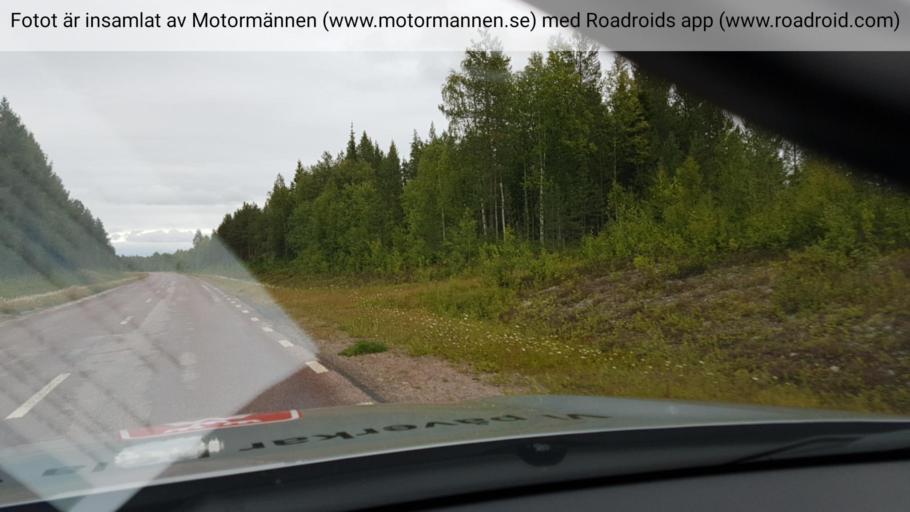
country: SE
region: Norrbotten
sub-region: Pajala Kommun
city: Pajala
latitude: 67.1456
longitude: 22.6217
